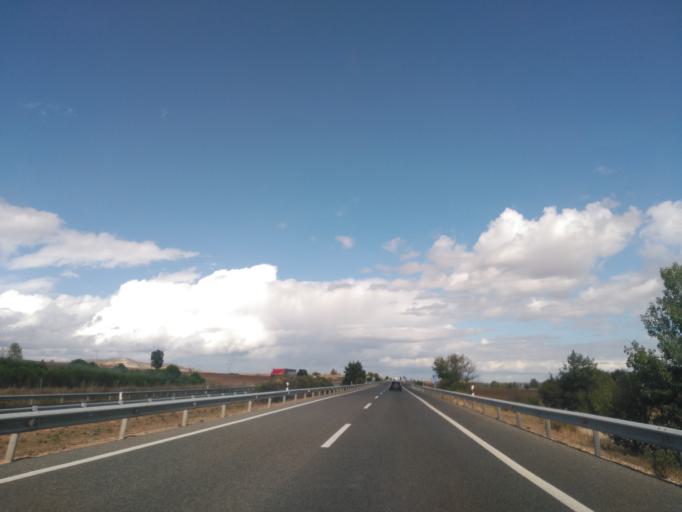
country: ES
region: Castille and Leon
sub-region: Provincia de Burgos
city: Villaldemiro
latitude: 42.2456
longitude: -3.9663
